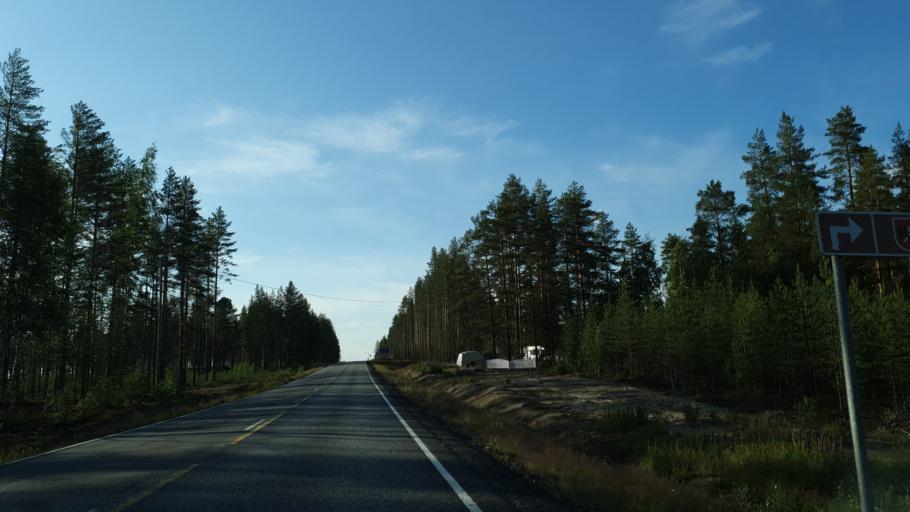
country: FI
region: Kainuu
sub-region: Kehys-Kainuu
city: Kuhmo
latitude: 64.0947
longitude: 29.4781
